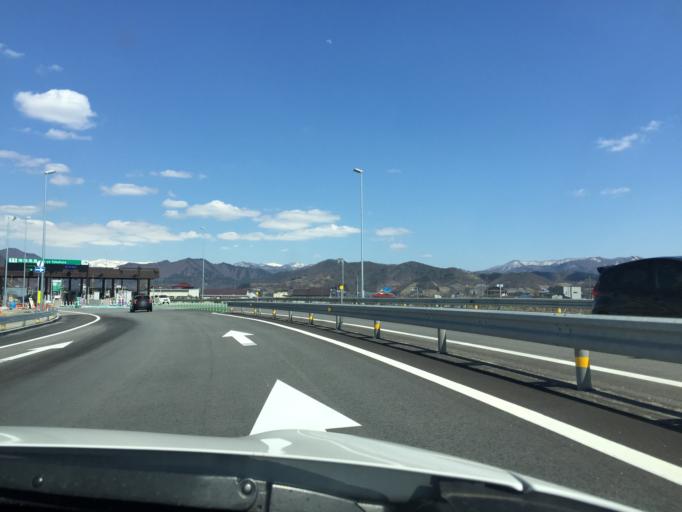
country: JP
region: Yamagata
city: Takahata
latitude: 38.0244
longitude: 140.1657
